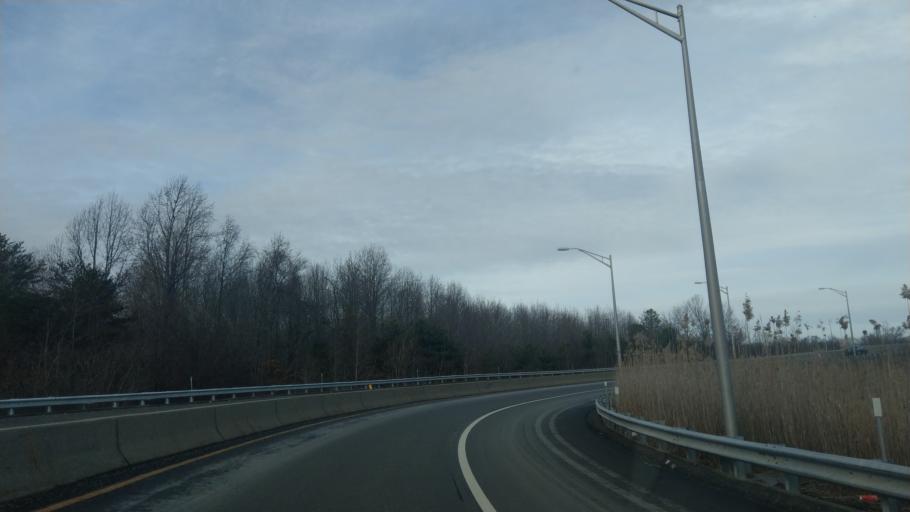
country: US
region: New Jersey
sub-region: Burlington County
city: Roebling
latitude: 40.0984
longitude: -74.7878
